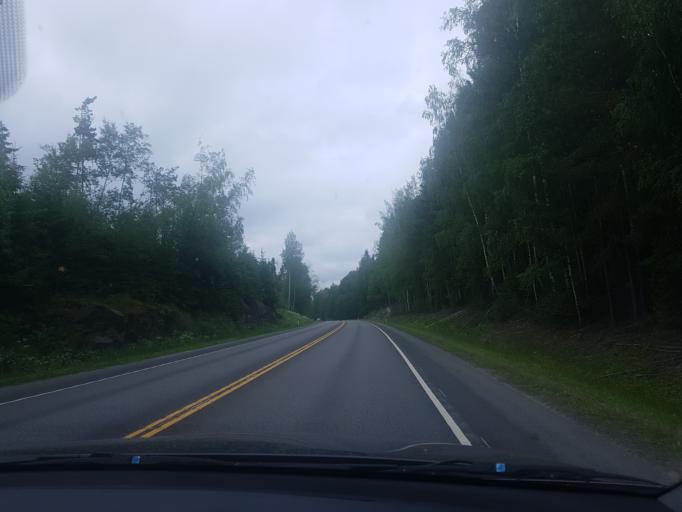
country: FI
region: Pirkanmaa
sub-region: Tampere
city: Paelkaene
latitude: 61.3963
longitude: 24.2101
